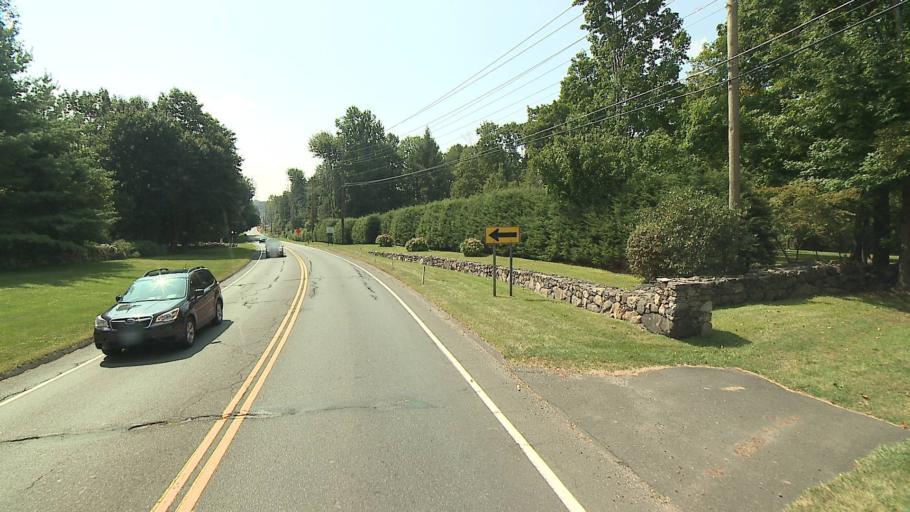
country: US
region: Connecticut
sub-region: Fairfield County
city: Ridgefield
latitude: 41.3019
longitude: -73.4921
